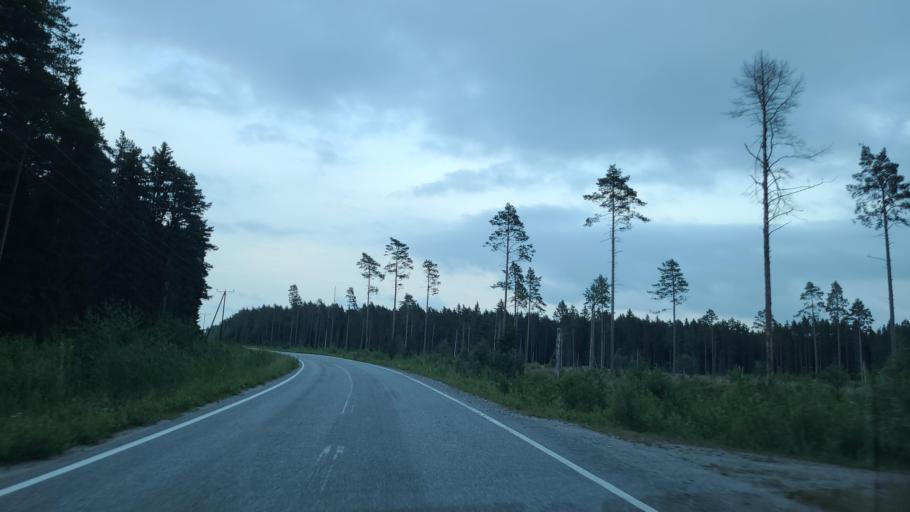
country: FI
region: Ostrobothnia
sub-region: Vaasa
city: Replot
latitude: 63.2040
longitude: 21.2715
